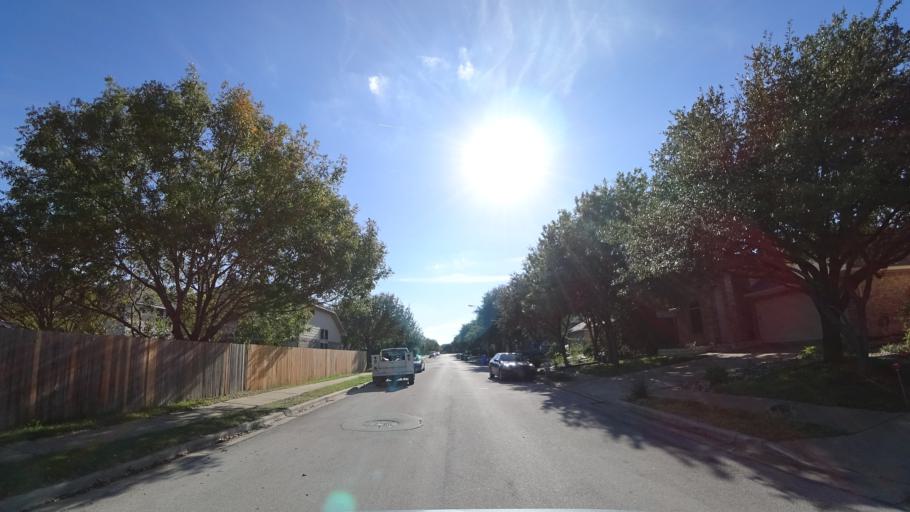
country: US
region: Texas
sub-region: Travis County
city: Wells Branch
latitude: 30.4623
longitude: -97.6838
